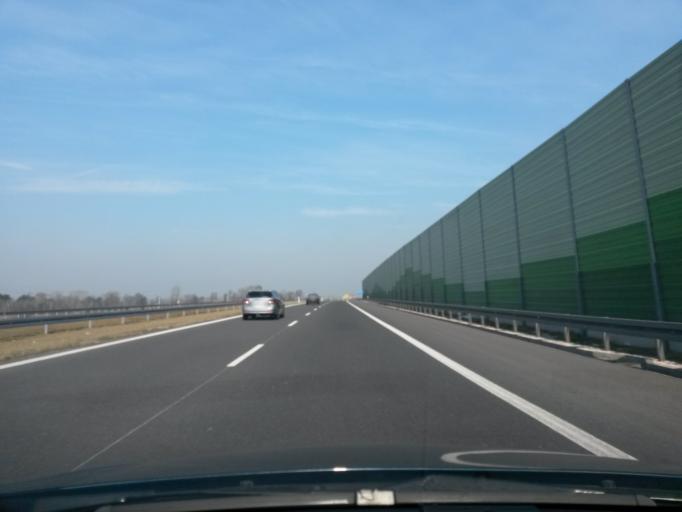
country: PL
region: Lodz Voivodeship
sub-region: Powiat leczycki
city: Piatek
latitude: 52.0938
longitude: 19.5183
